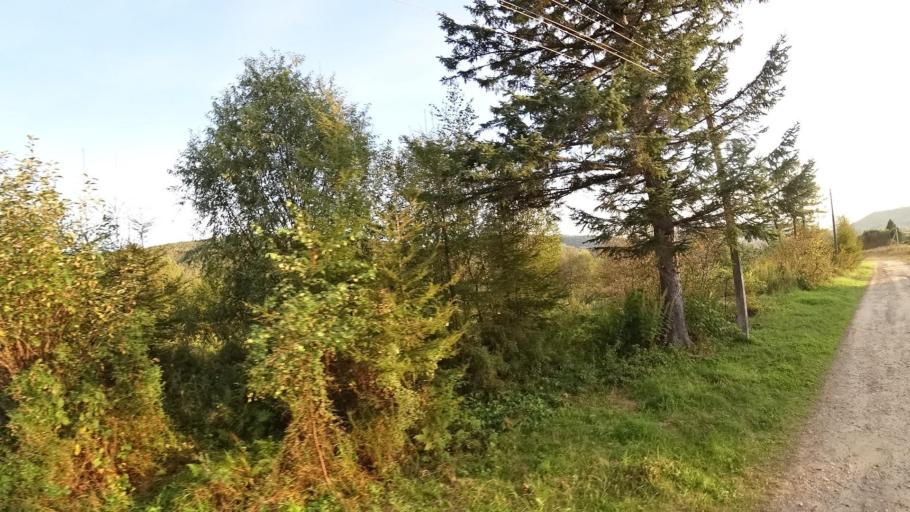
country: RU
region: Jewish Autonomous Oblast
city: Kul'dur
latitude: 49.2095
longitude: 131.6480
